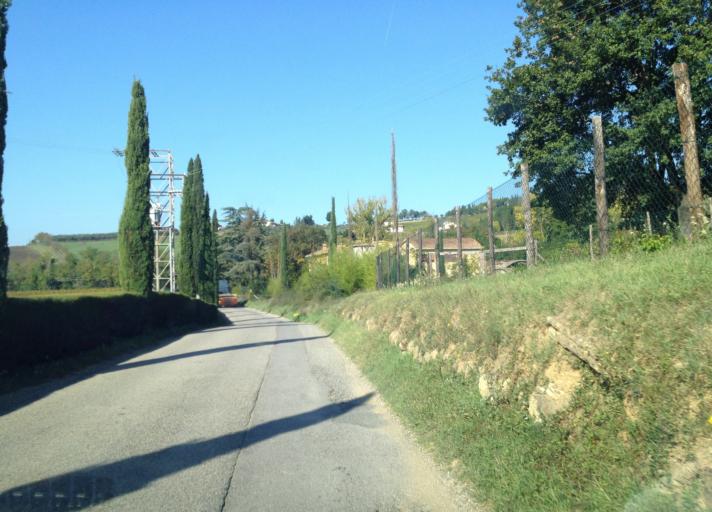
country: IT
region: Tuscany
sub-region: Provincia di Siena
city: Poggibonsi
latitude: 43.4898
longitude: 11.1766
